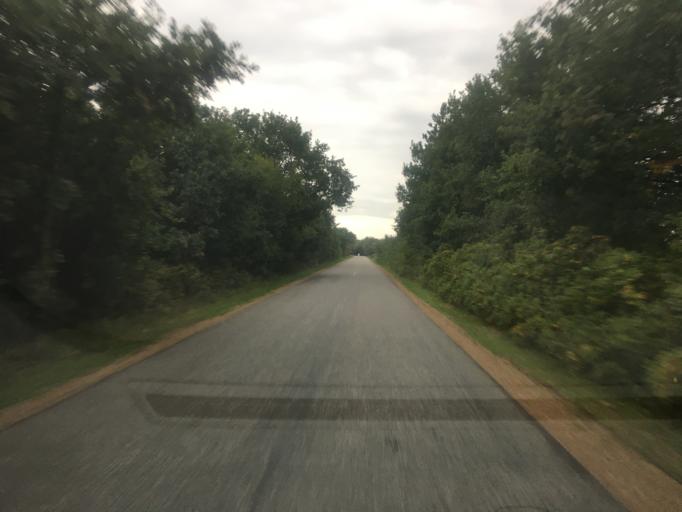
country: DK
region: South Denmark
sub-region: Tonder Kommune
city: Logumkloster
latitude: 55.0187
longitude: 9.0351
